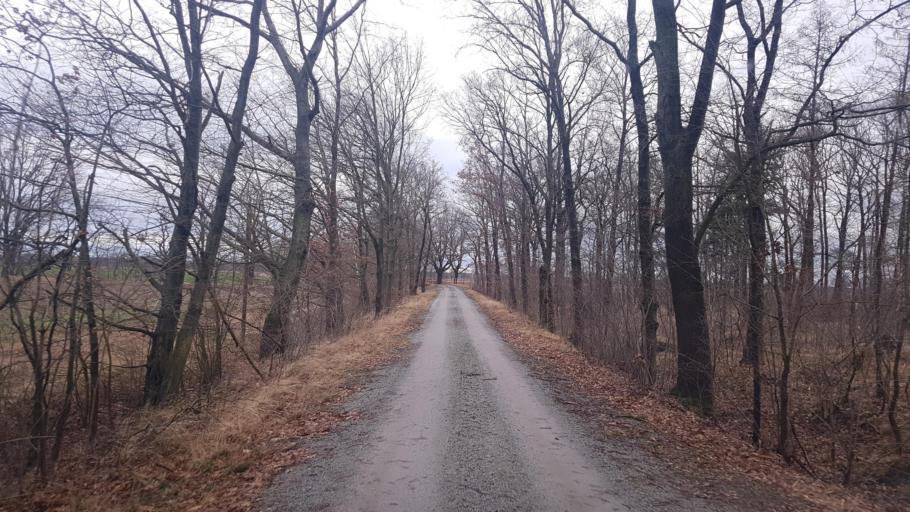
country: DE
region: Brandenburg
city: Plessa
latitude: 51.4469
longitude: 13.6518
